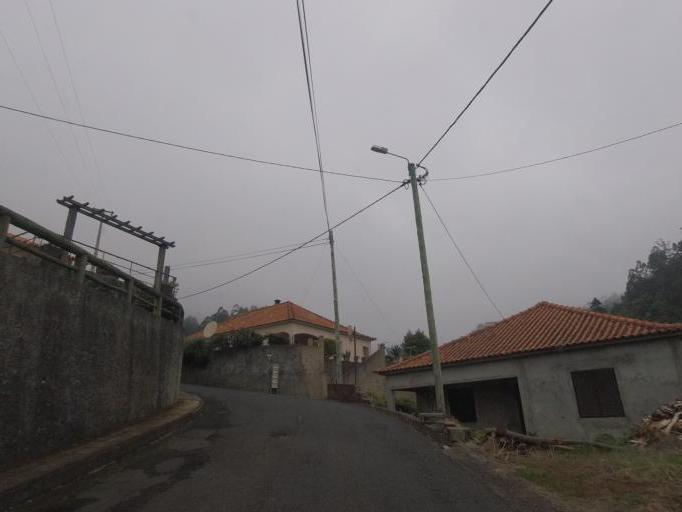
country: PT
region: Madeira
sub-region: Santa Cruz
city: Santa Cruz
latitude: 32.7336
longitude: -16.8226
